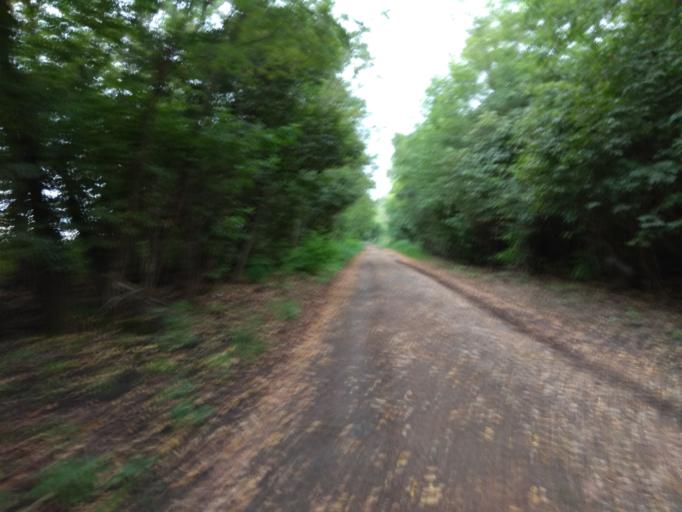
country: HU
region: Borsod-Abauj-Zemplen
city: Monok
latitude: 48.1750
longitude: 21.1207
